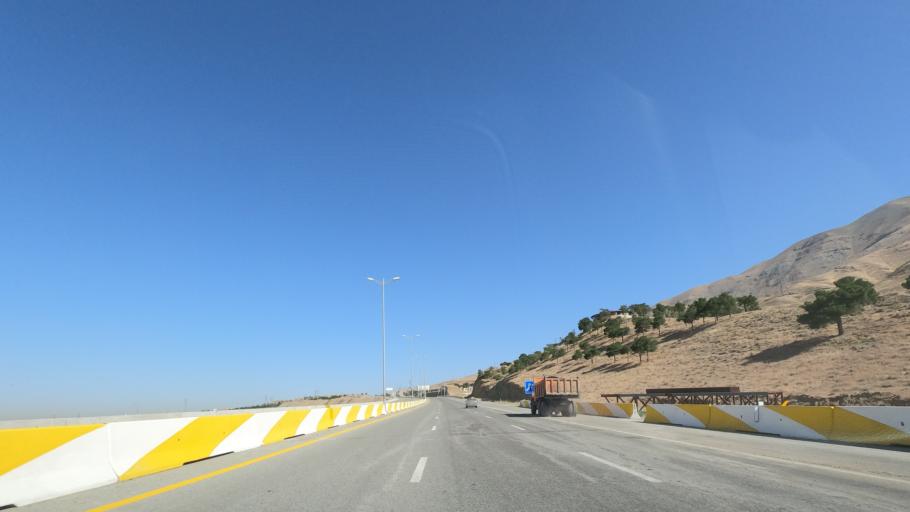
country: IR
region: Tehran
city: Shahr-e Qods
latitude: 35.7595
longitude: 51.0765
